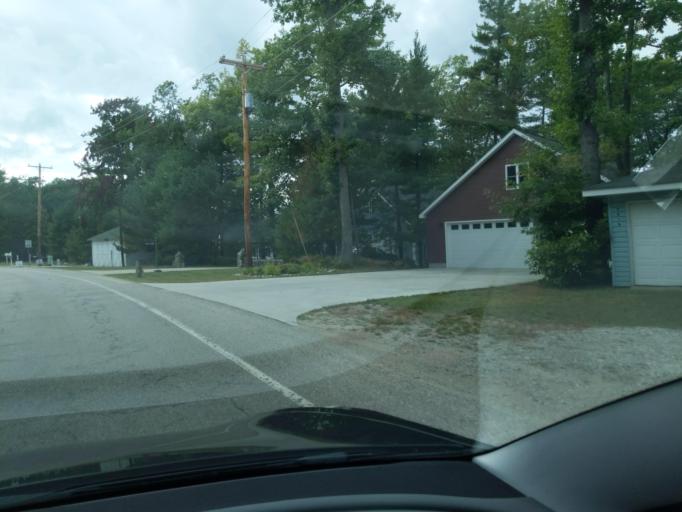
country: US
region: Michigan
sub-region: Kalkaska County
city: Rapid City
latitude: 44.8597
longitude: -85.2885
